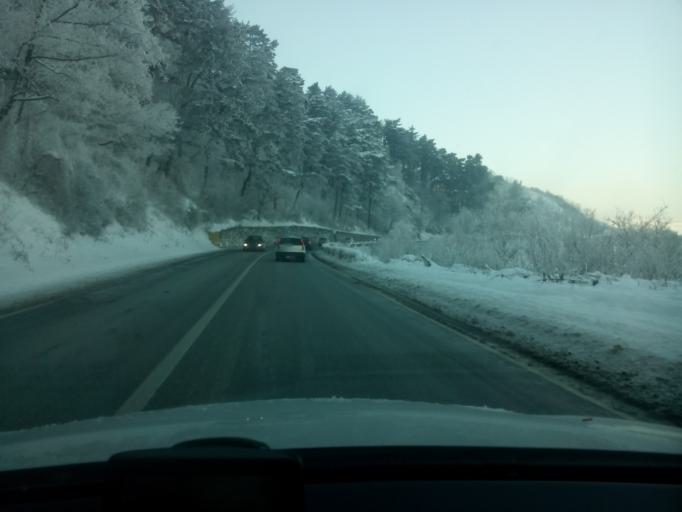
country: RO
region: Sibiu
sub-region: Comuna Boita
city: Boita
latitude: 45.6248
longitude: 24.2629
